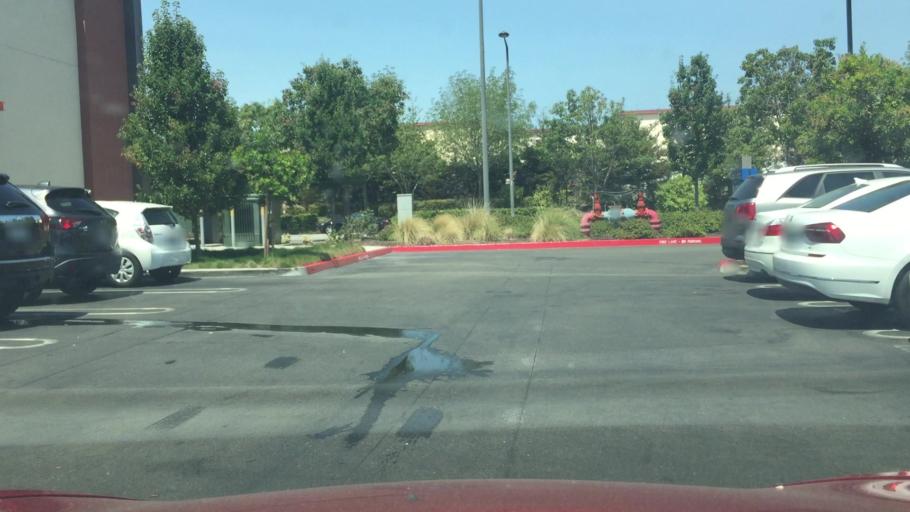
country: US
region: California
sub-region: Alameda County
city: Fremont
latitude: 37.5022
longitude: -121.9699
